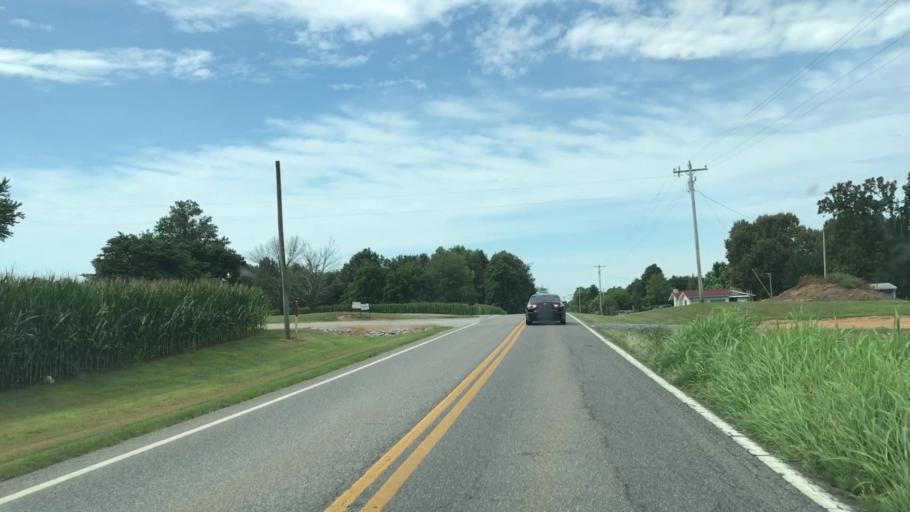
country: US
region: Kentucky
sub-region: Graves County
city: Mayfield
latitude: 36.8495
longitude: -88.5743
